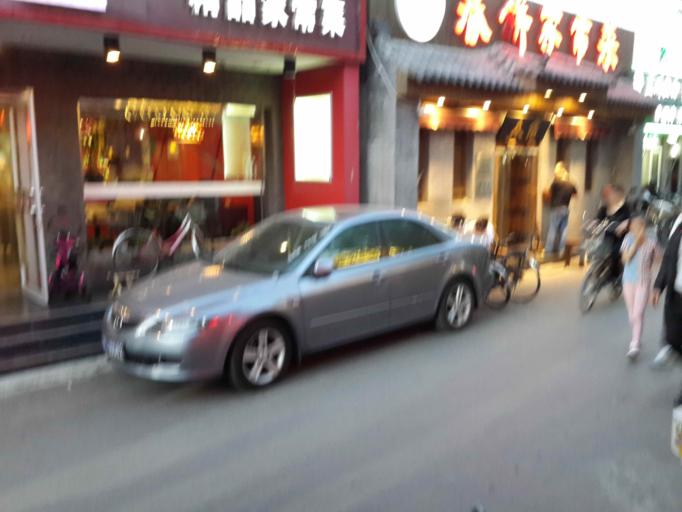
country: CN
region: Beijing
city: Jingshan
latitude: 39.9205
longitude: 116.4118
